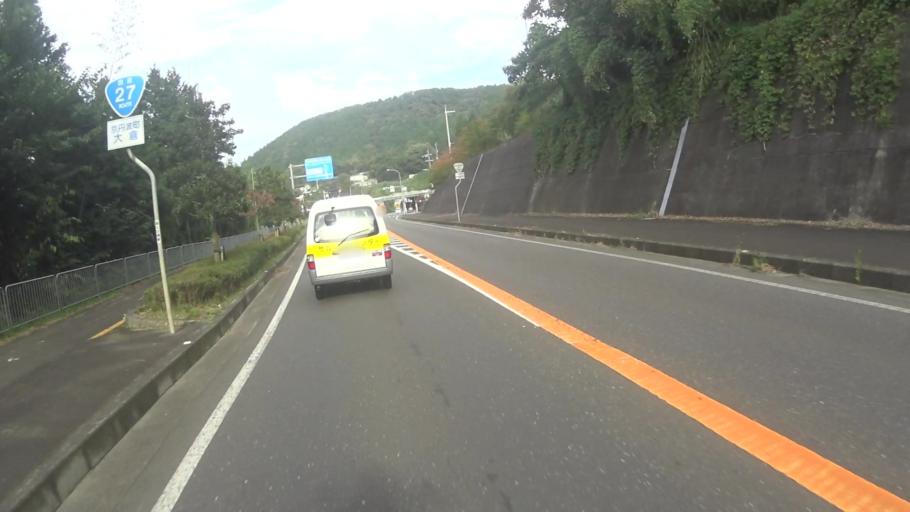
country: JP
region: Kyoto
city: Ayabe
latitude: 35.2603
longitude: 135.4093
